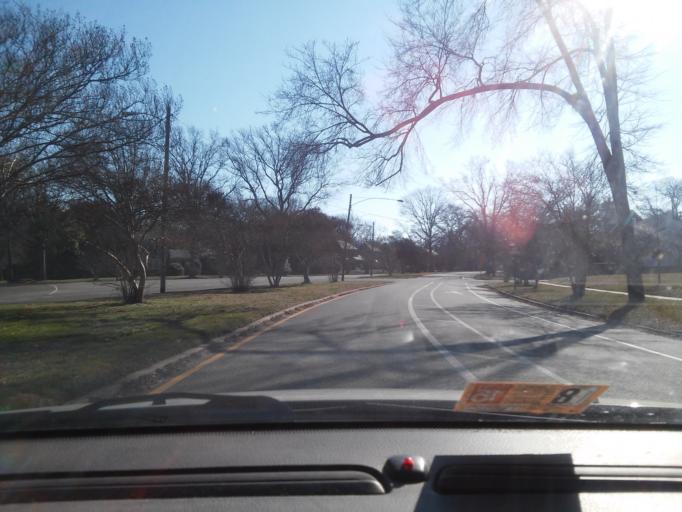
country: US
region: Virginia
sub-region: City of Richmond
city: Richmond
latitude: 37.5750
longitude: -77.4558
